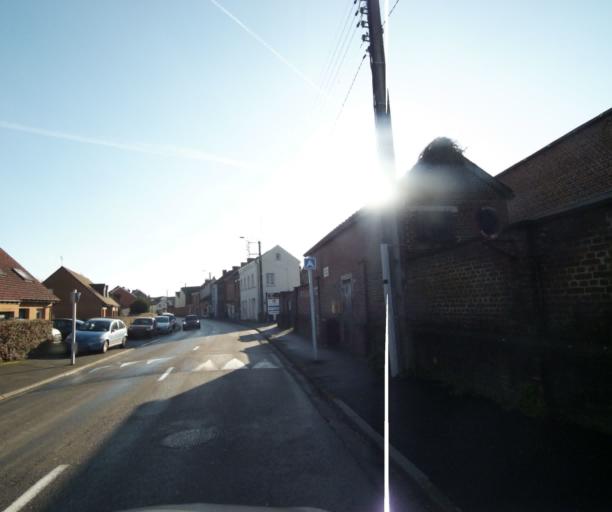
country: FR
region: Nord-Pas-de-Calais
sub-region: Departement du Nord
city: Marly
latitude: 50.3460
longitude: 3.5436
